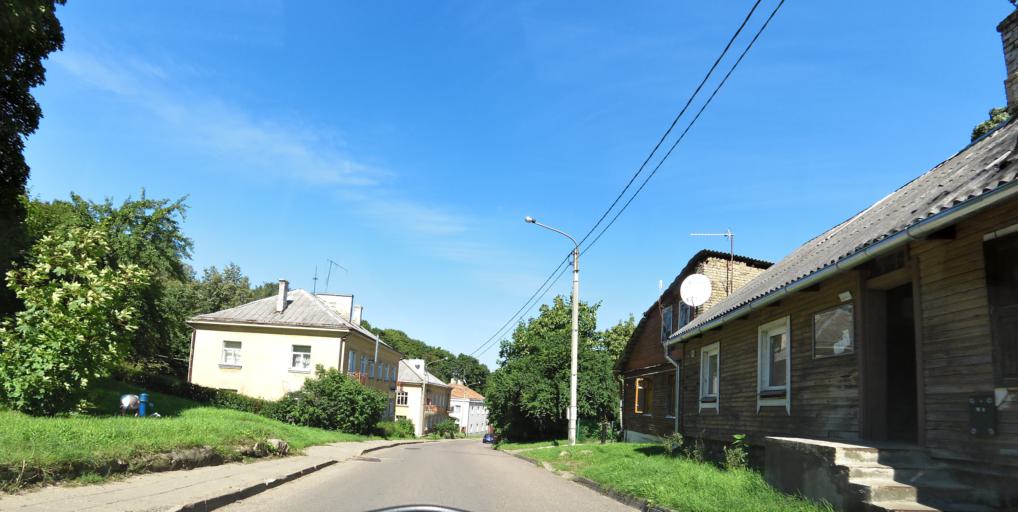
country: LT
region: Vilnius County
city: Naujamiestis
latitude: 54.6660
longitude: 25.2894
